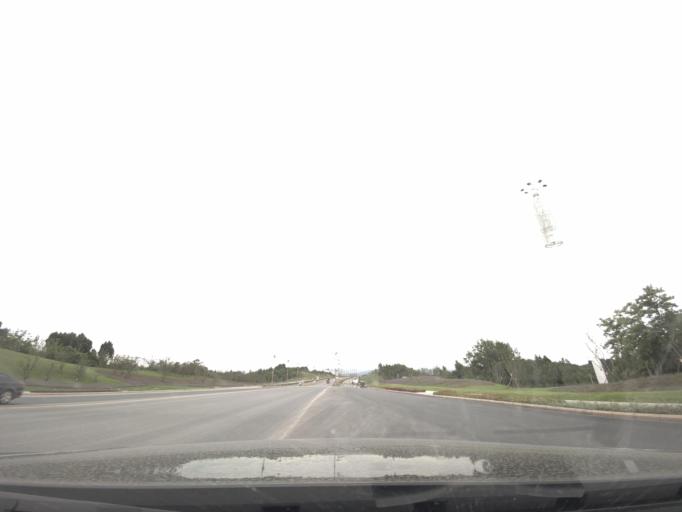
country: CN
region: Sichuan
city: Jiancheng
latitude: 30.3093
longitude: 104.3400
